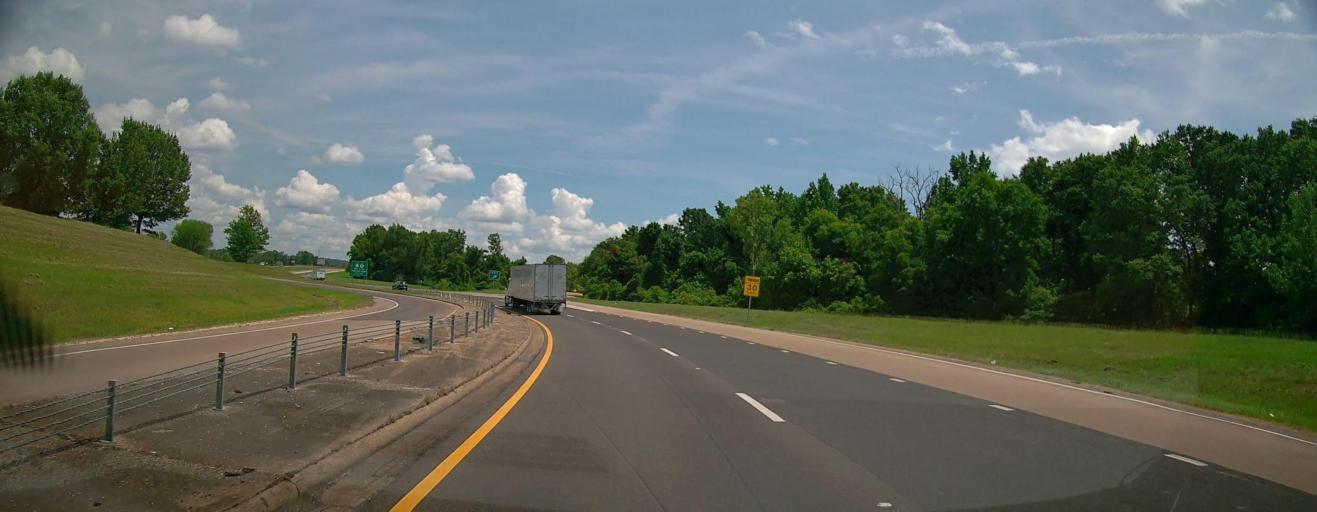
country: US
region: Mississippi
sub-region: Lee County
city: Tupelo
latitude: 34.2745
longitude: -88.7068
